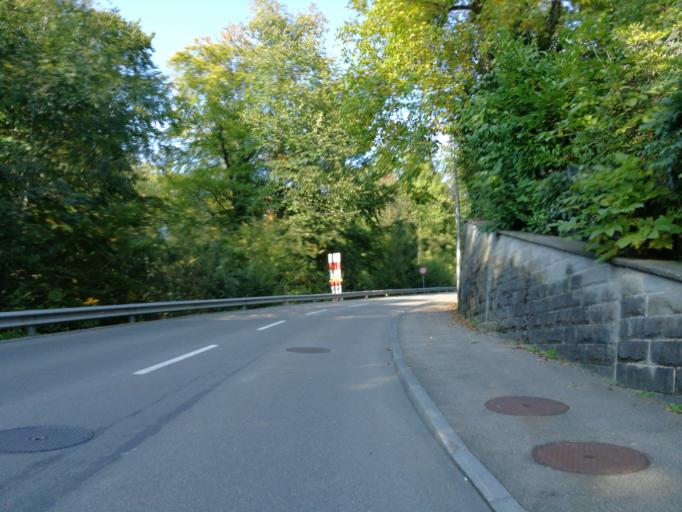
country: CH
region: Zurich
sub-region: Bezirk Meilen
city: Dorf
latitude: 47.2415
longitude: 8.7395
